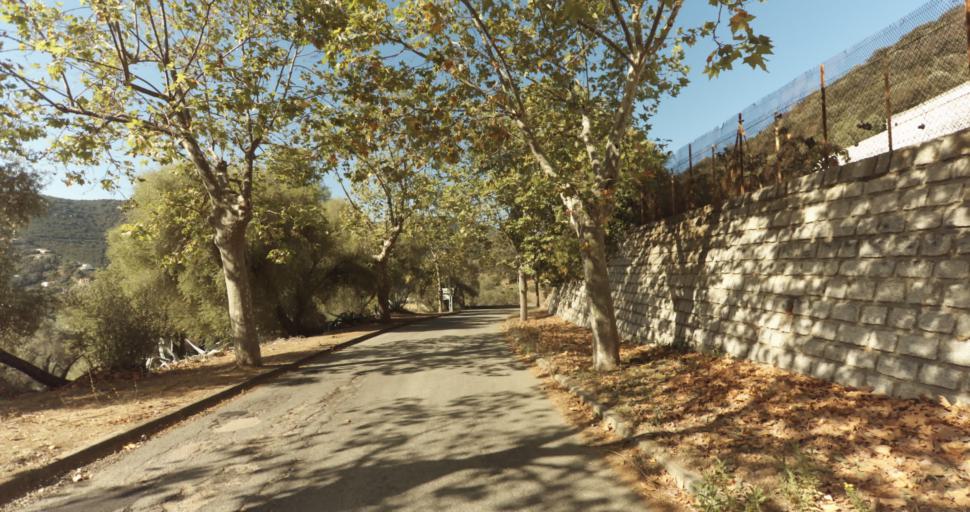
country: FR
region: Corsica
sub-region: Departement de la Corse-du-Sud
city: Ajaccio
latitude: 41.9347
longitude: 8.7129
